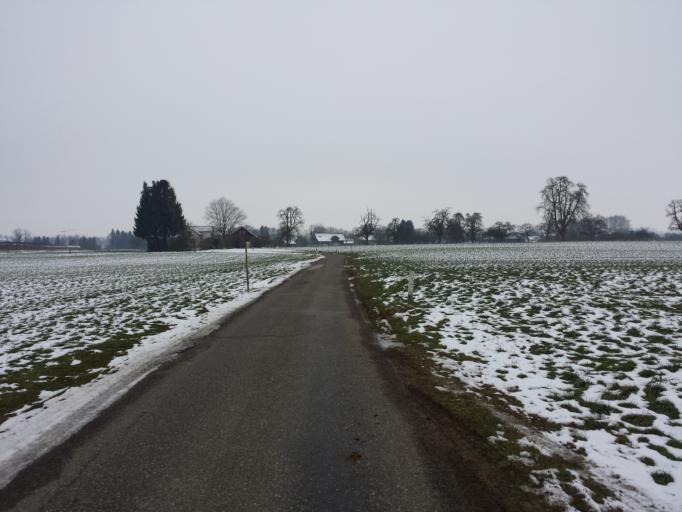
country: CH
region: Thurgau
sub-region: Arbon District
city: Egnach
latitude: 47.5460
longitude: 9.3699
